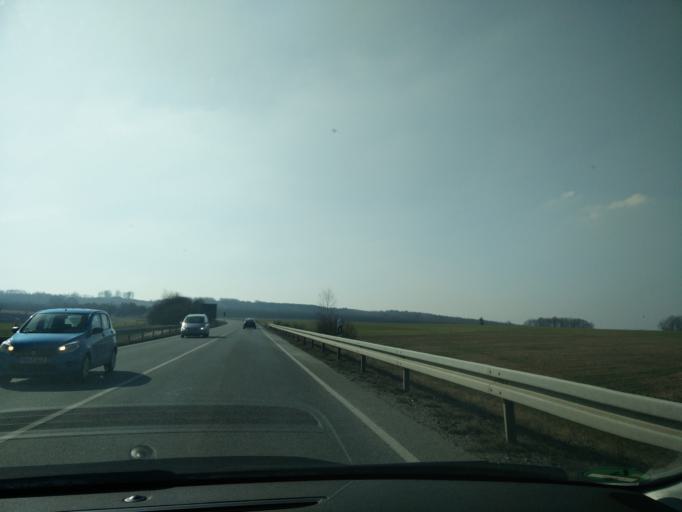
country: DE
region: Saxony
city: Hartmannsdorf
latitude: 50.8909
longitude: 12.7875
